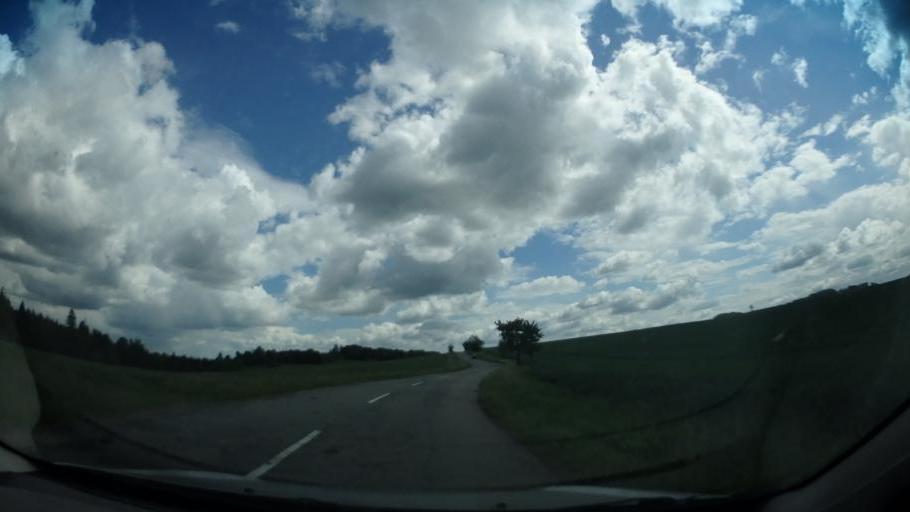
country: CZ
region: South Moravian
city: Velke Opatovice
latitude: 49.6212
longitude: 16.6036
